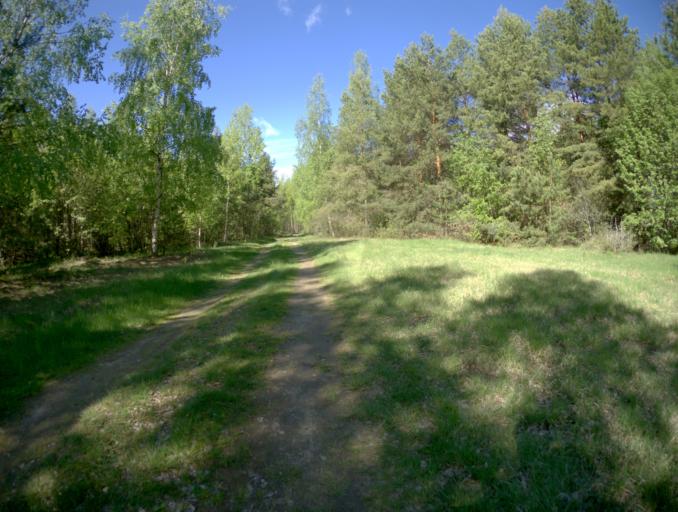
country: RU
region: Rjazan
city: Spas-Klepiki
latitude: 55.2487
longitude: 40.1039
